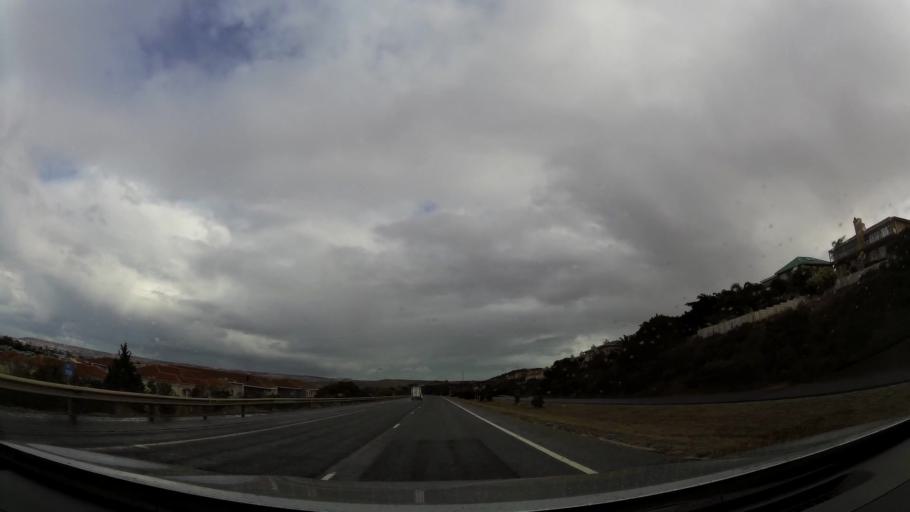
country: ZA
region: Western Cape
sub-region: Eden District Municipality
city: Mossel Bay
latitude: -34.1274
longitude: 22.1039
